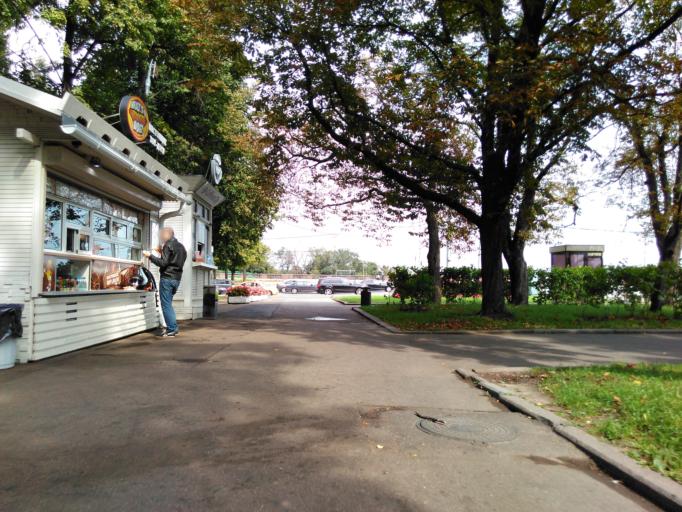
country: RU
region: Moscow
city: Vorob'yovo
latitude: 55.7091
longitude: 37.5400
